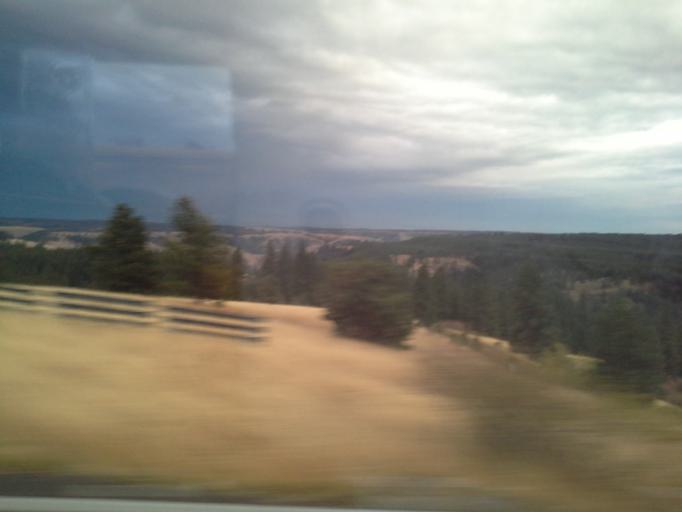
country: US
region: Oregon
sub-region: Umatilla County
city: Mission
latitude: 45.5843
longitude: -118.5778
